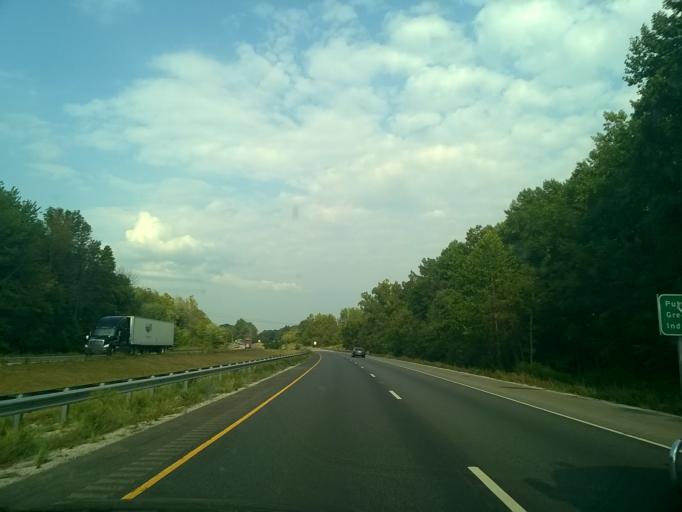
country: US
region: Indiana
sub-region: Clay County
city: Brazil
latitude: 39.4497
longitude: -87.1116
